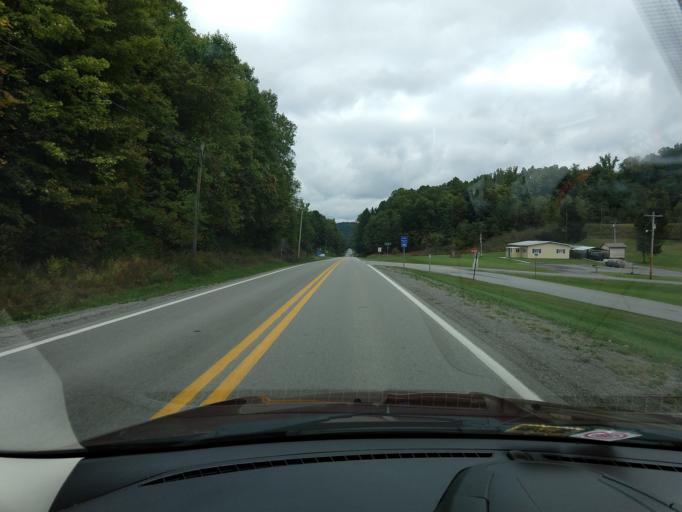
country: US
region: West Virginia
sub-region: Barbour County
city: Philippi
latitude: 39.1122
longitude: -79.9952
